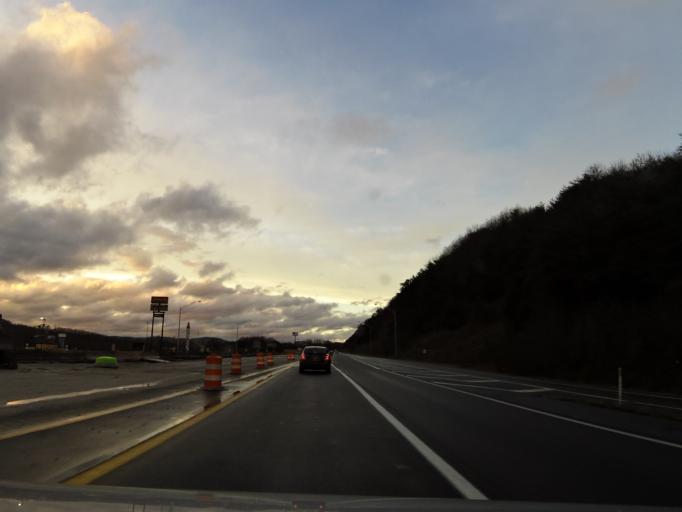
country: US
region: Tennessee
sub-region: Campbell County
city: Jacksboro
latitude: 36.3790
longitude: -84.2462
